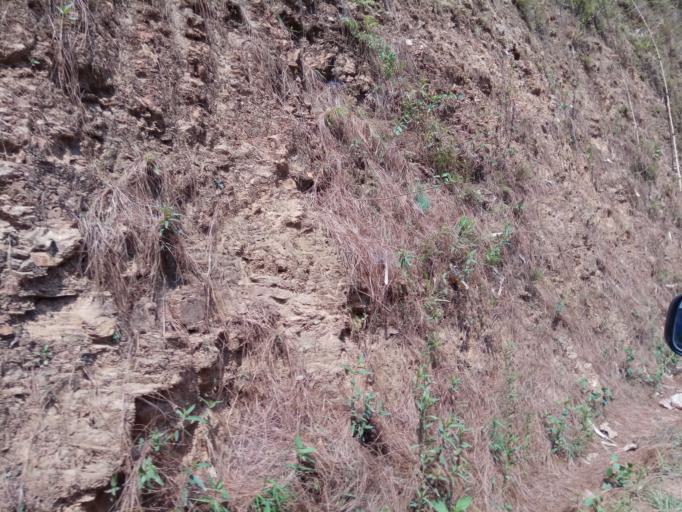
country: NP
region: Central Region
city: Kirtipur
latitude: 27.8945
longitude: 85.0768
